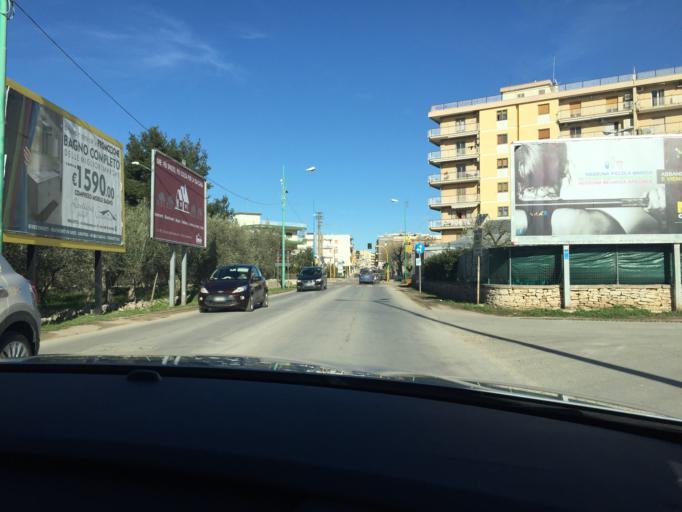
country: IT
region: Apulia
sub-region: Provincia di Bari
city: Terlizzi
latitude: 41.1316
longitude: 16.5336
